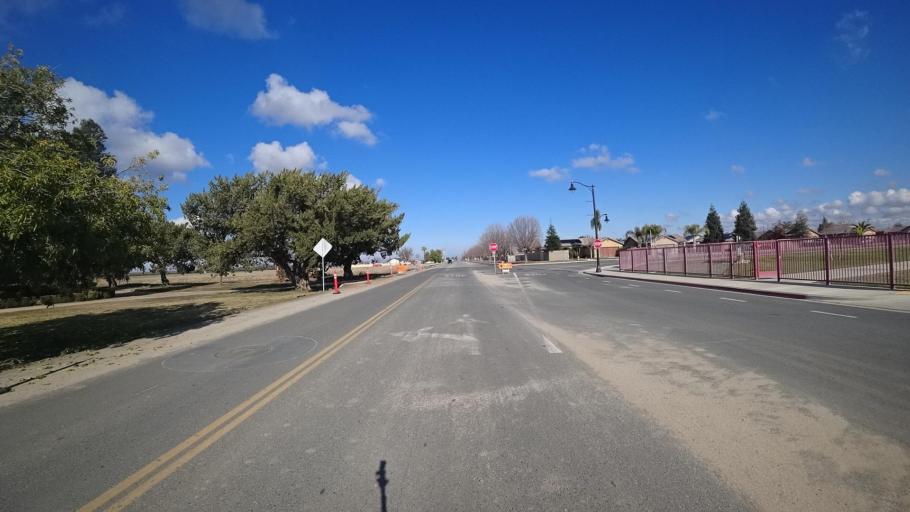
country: US
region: California
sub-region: Kern County
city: McFarland
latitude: 35.6667
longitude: -119.2410
